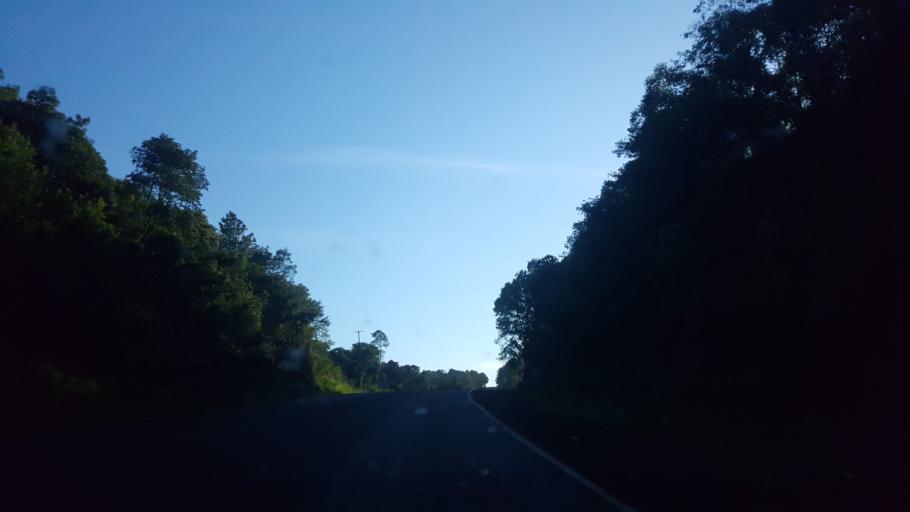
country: AR
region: Misiones
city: Caraguatay
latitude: -26.6646
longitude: -54.7560
